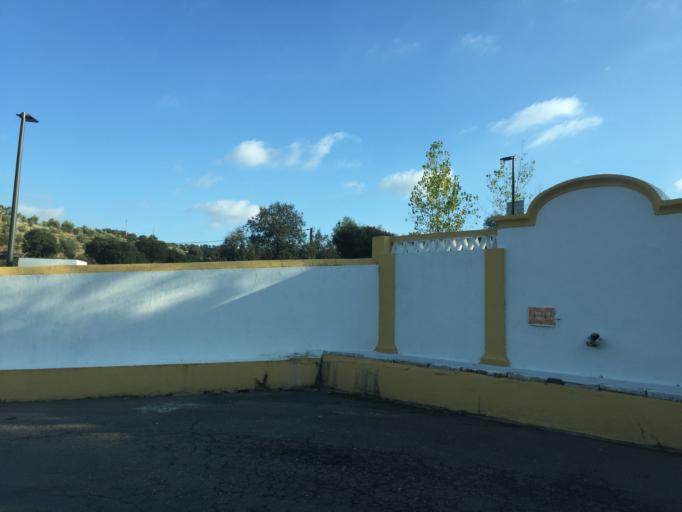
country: PT
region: Portalegre
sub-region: Fronteira
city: Fronteira
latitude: 39.0698
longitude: -7.6505
